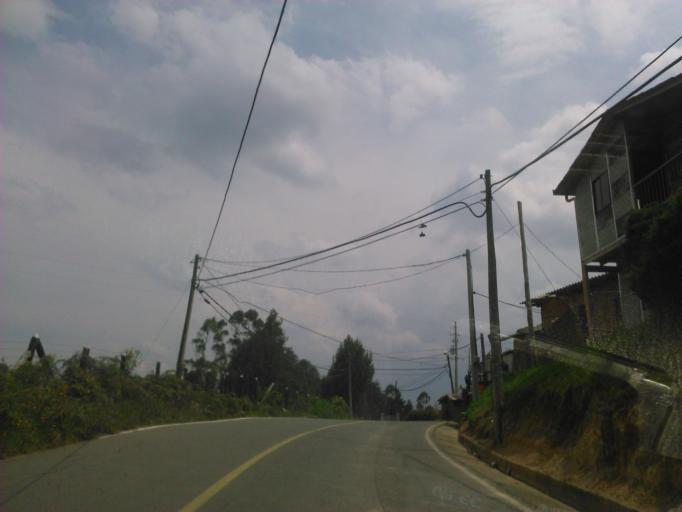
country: CO
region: Antioquia
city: San Vicente
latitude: 6.2362
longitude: -75.3772
